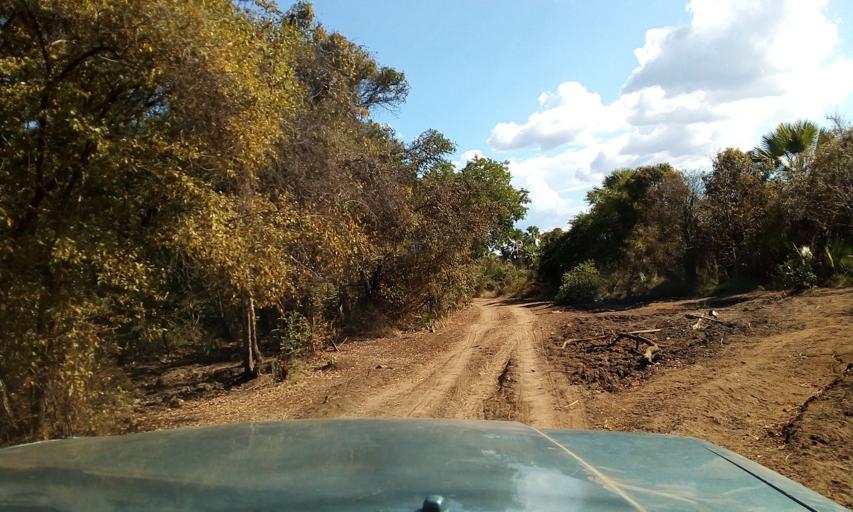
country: MG
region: Boeny
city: Mahajanga
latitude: -16.0606
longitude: 45.7960
